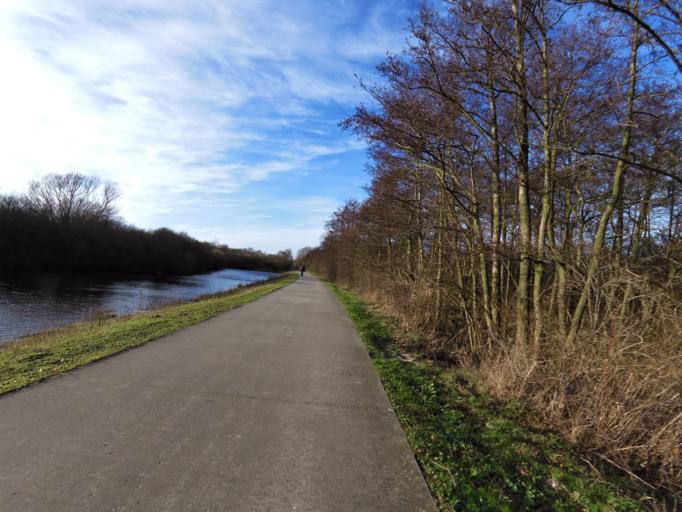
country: NL
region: South Holland
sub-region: Gemeente Rotterdam
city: Hoek van Holland
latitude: 51.9141
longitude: 4.0702
